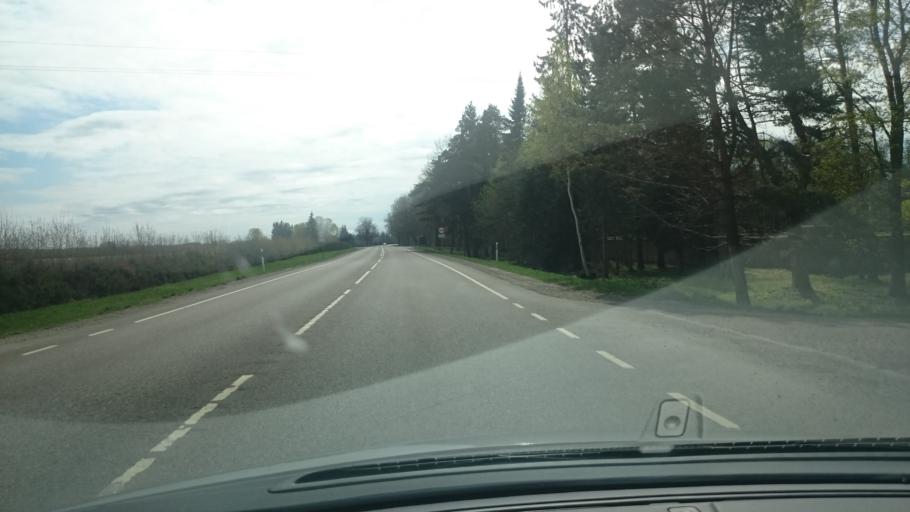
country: EE
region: Laeaene-Virumaa
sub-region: Rakvere linn
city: Rakvere
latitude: 59.3966
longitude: 26.3788
